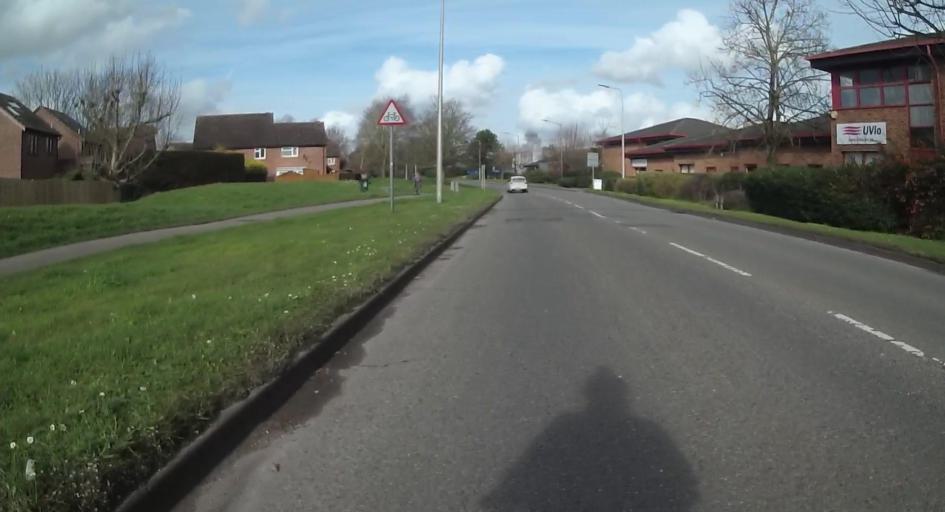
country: GB
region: England
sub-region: West Berkshire
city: Thatcham
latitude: 51.3982
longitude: -1.2386
